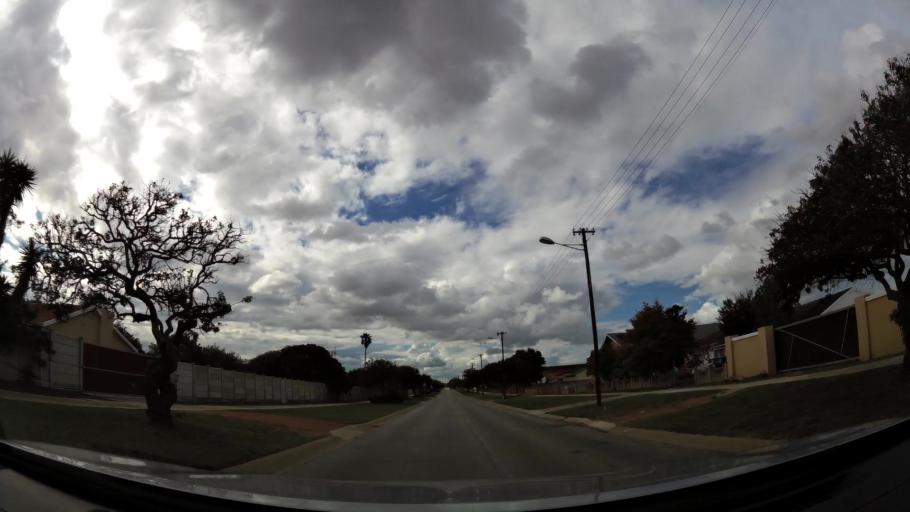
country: ZA
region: Eastern Cape
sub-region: Nelson Mandela Bay Metropolitan Municipality
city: Port Elizabeth
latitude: -33.9383
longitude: 25.5224
